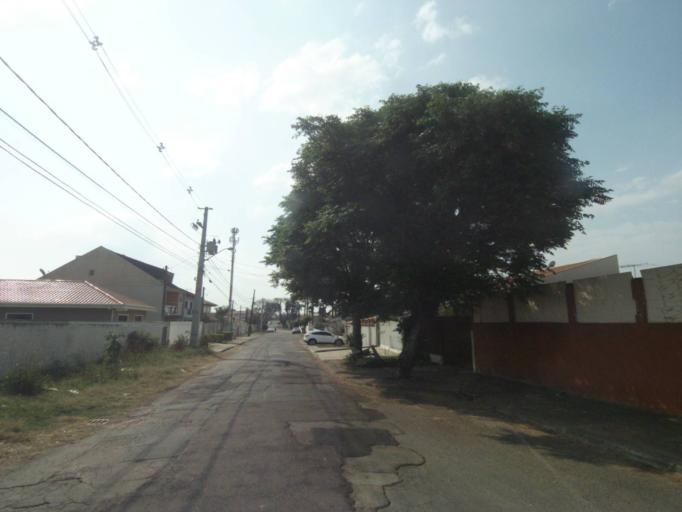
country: BR
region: Parana
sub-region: Sao Jose Dos Pinhais
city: Sao Jose dos Pinhais
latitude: -25.5165
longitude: -49.2440
